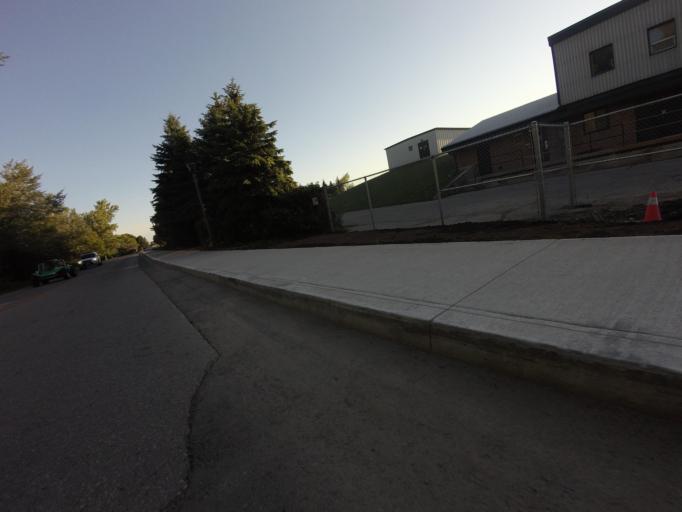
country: CA
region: Ontario
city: Goderich
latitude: 43.7394
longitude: -81.7260
